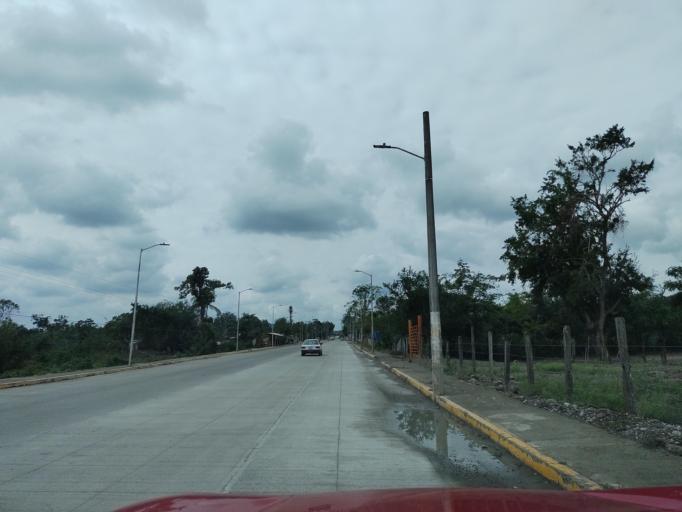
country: MX
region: Veracruz
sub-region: Papantla
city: El Chote
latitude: 20.4328
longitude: -97.3744
